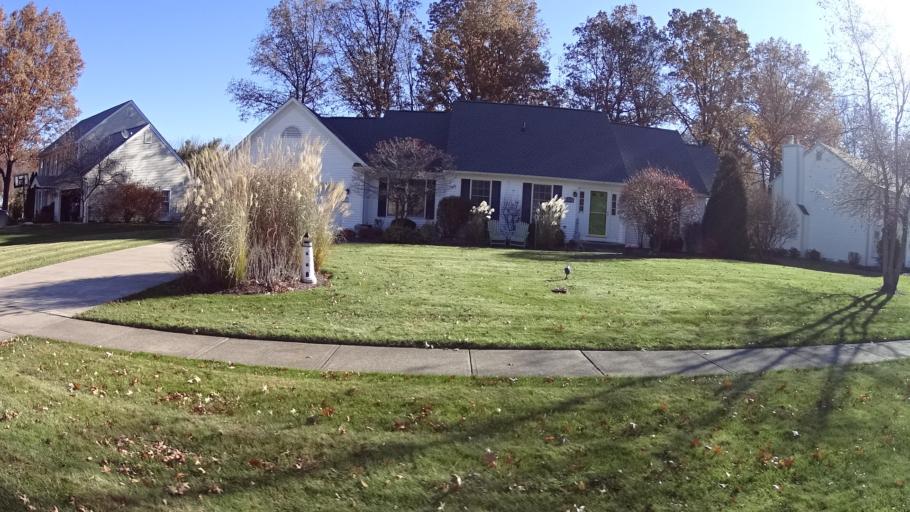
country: US
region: Ohio
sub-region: Lorain County
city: Avon Lake
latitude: 41.4947
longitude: -81.9945
